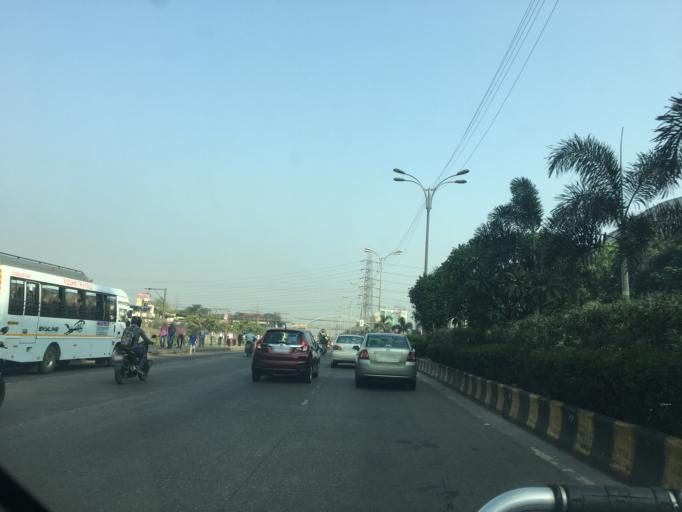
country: IN
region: Maharashtra
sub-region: Thane
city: Airoli
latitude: 19.1634
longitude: 72.9999
